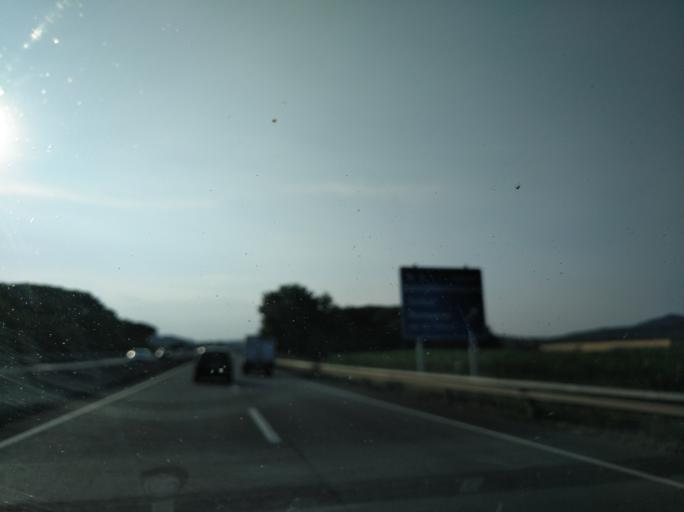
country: ES
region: Catalonia
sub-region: Provincia de Girona
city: Santa Cristina d'Aro
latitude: 41.8164
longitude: 2.9841
